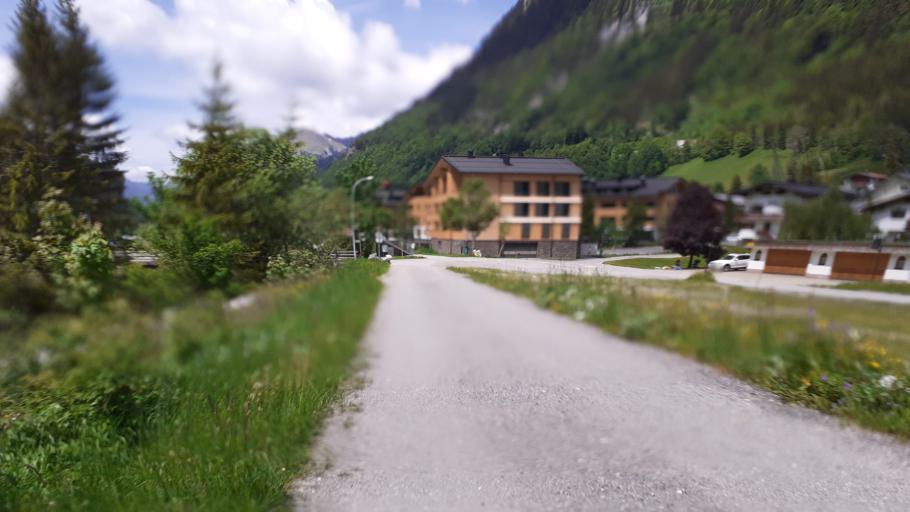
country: AT
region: Vorarlberg
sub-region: Politischer Bezirk Bludenz
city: Klosterle
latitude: 47.1305
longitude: 10.0950
